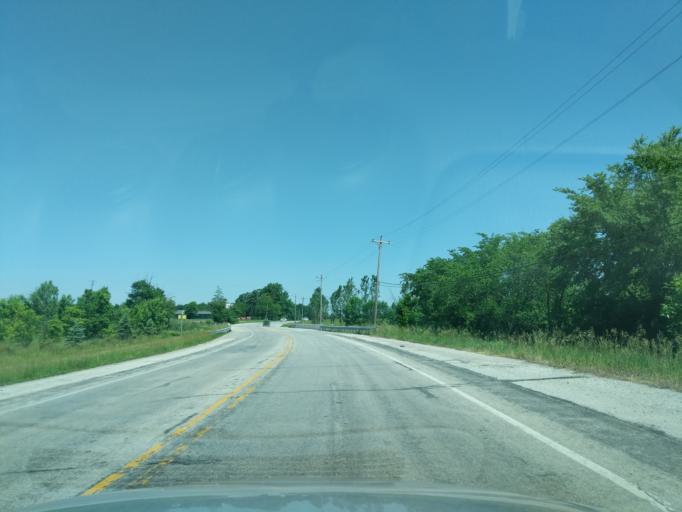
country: US
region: Indiana
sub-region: Whitley County
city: Columbia City
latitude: 41.0883
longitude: -85.4703
